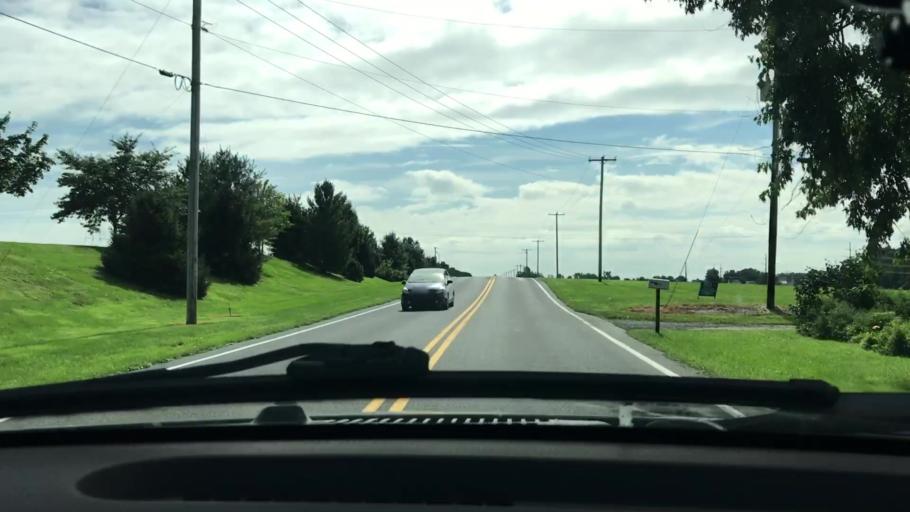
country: US
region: Pennsylvania
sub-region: Lancaster County
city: Manheim
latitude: 40.1391
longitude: -76.4056
